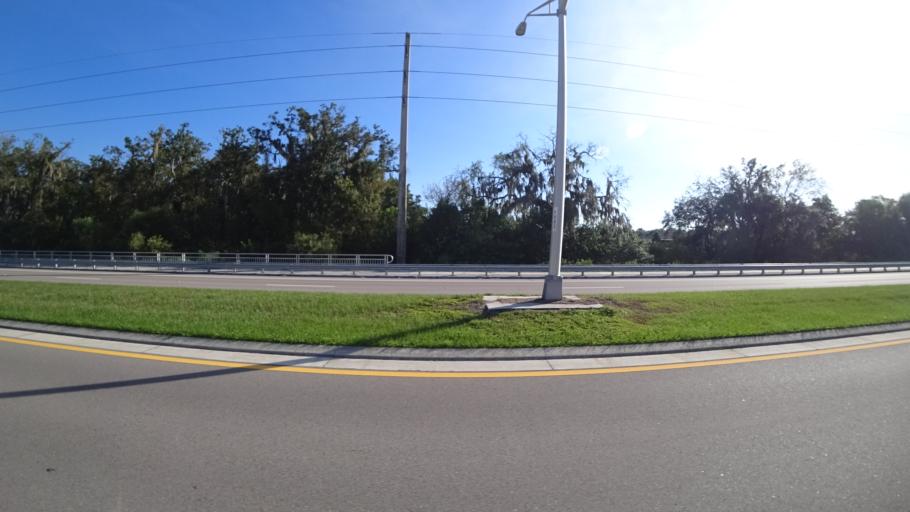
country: US
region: Florida
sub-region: Manatee County
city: Samoset
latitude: 27.4615
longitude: -82.5185
